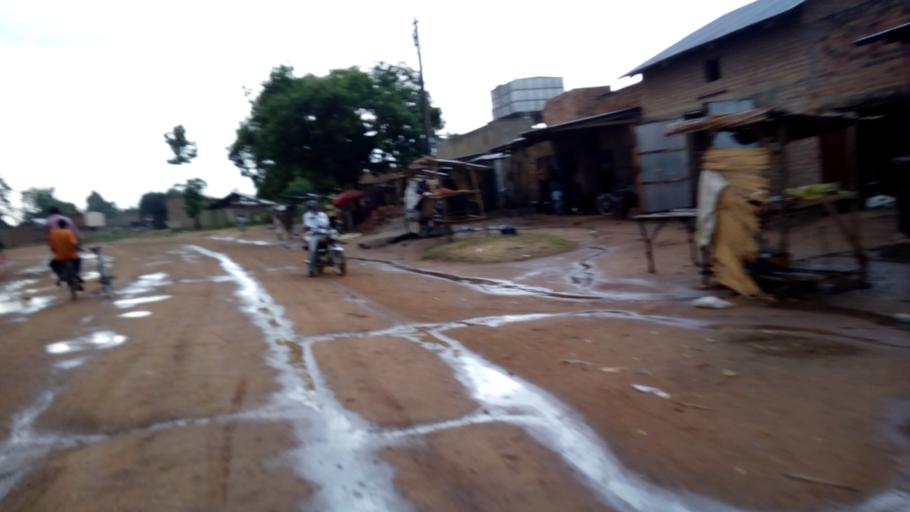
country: UG
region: Eastern Region
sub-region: Mbale District
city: Mbale
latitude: 1.0756
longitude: 34.0952
